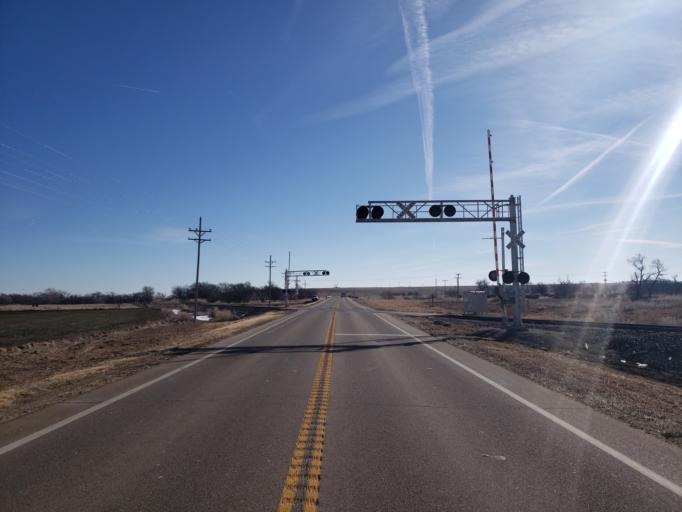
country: US
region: Kansas
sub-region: Ness County
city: Ness City
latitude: 38.4534
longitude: -99.6481
